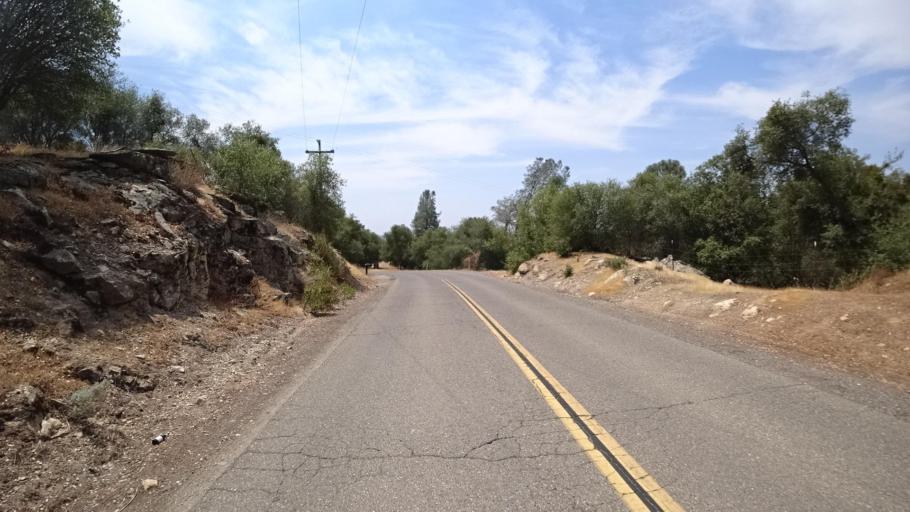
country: US
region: California
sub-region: Madera County
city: Ahwahnee
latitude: 37.4243
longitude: -119.8172
